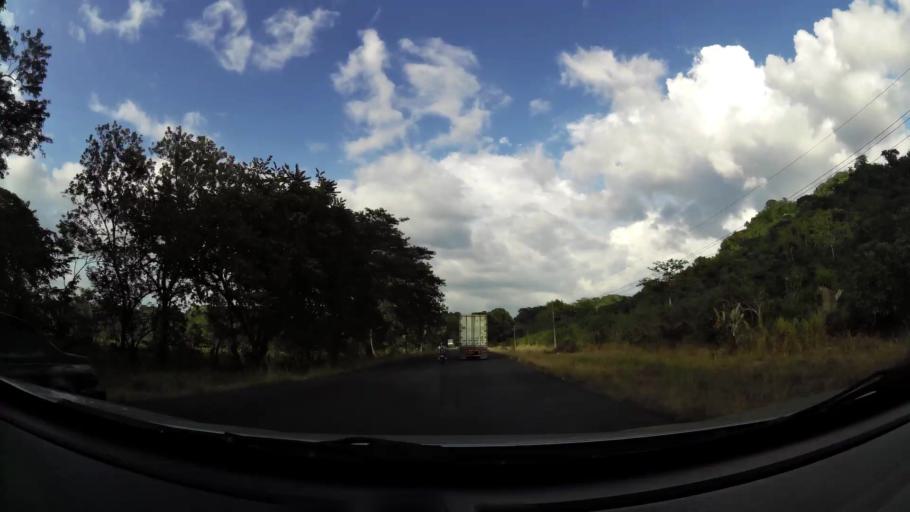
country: CR
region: Puntarenas
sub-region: Canton de Garabito
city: Jaco
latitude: 9.7600
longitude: -84.6167
